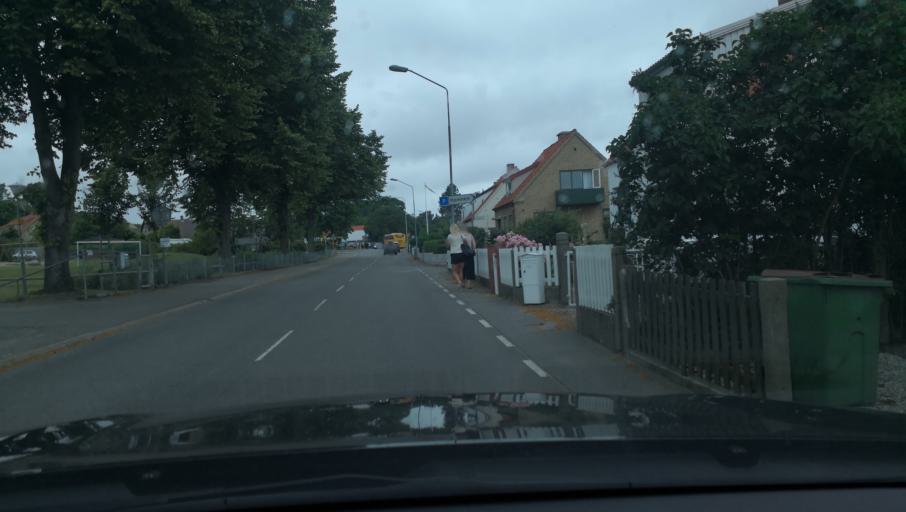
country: SE
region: Skane
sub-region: Simrishamns Kommun
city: Kivik
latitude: 55.6844
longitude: 14.2288
